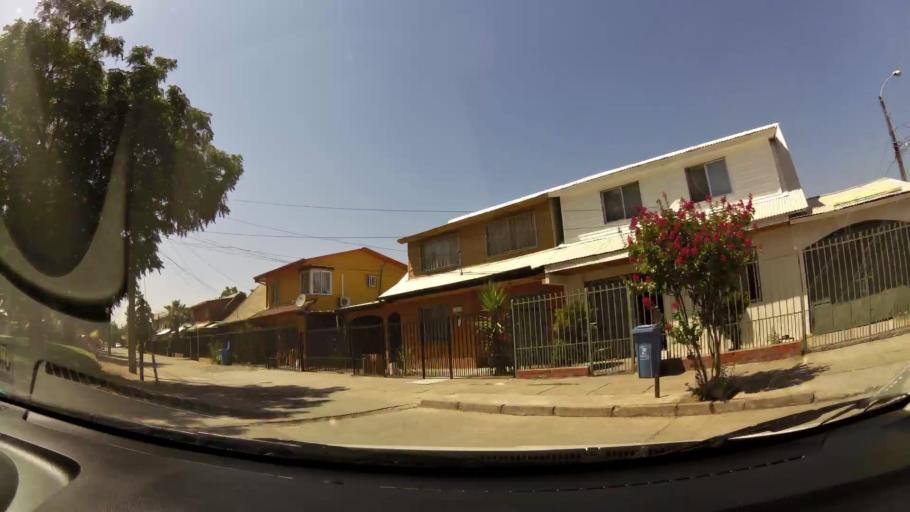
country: CL
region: Maule
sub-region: Provincia de Talca
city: Talca
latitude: -35.4244
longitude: -71.6286
